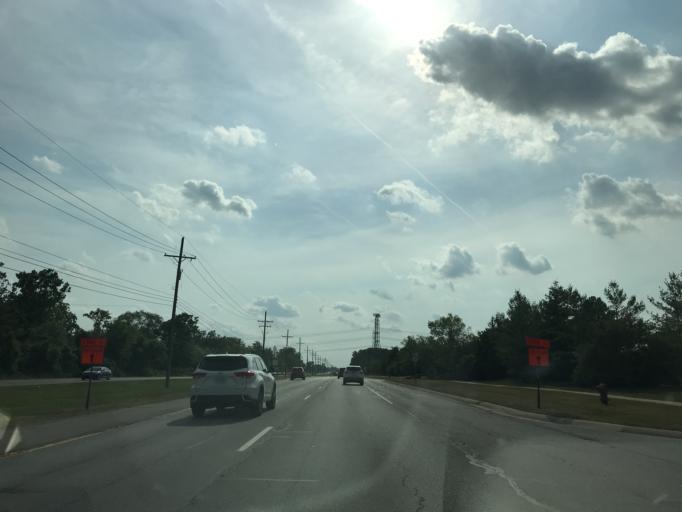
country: US
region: Michigan
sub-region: Wayne County
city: Canton
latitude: 42.2774
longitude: -83.4561
